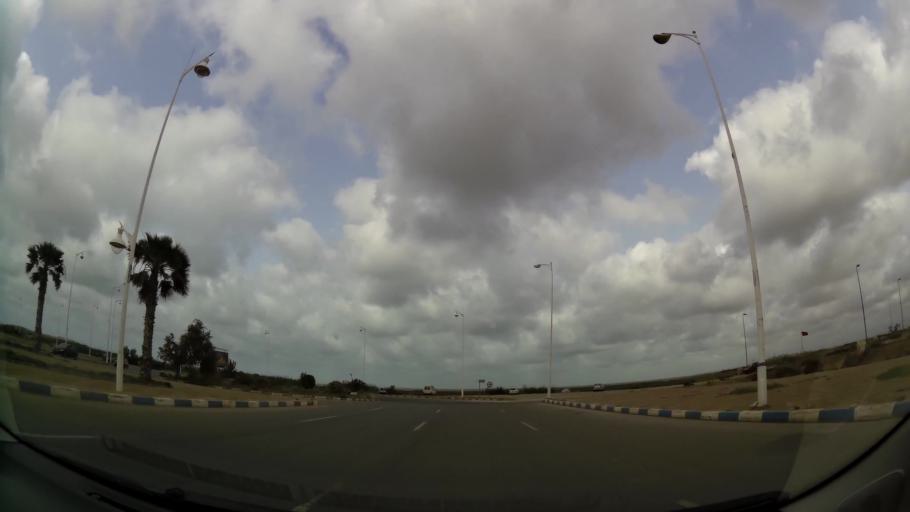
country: MA
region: Oriental
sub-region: Nador
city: Nador
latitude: 35.1537
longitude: -2.9104
